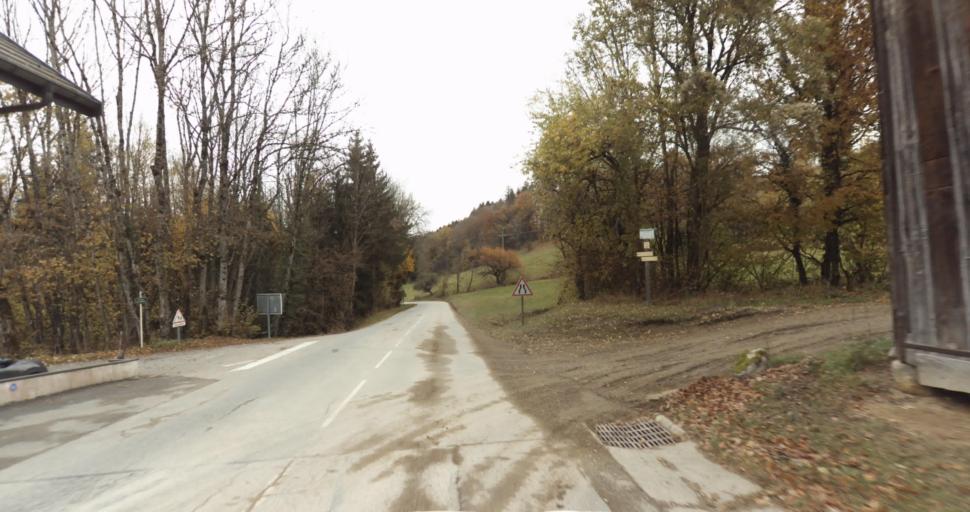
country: FR
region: Rhone-Alpes
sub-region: Departement de la Haute-Savoie
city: Saint-Jorioz
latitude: 45.8036
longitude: 6.1469
